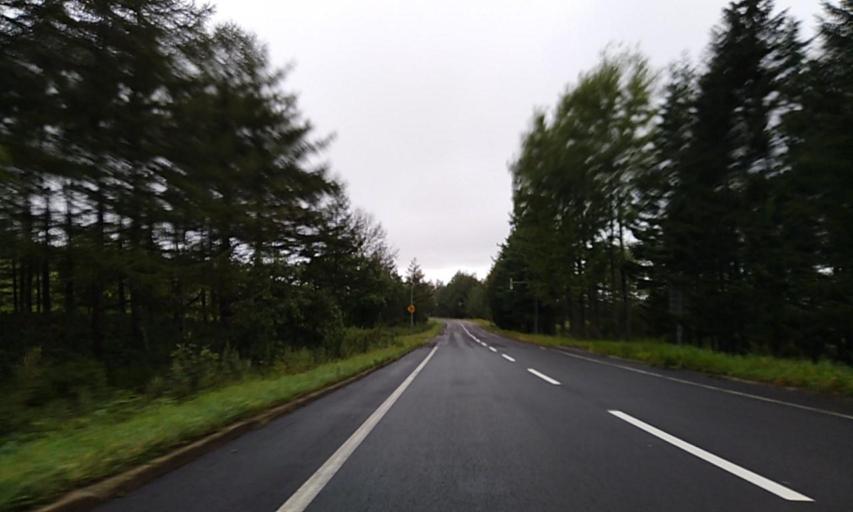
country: JP
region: Hokkaido
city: Kushiro
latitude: 43.4827
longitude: 144.5385
